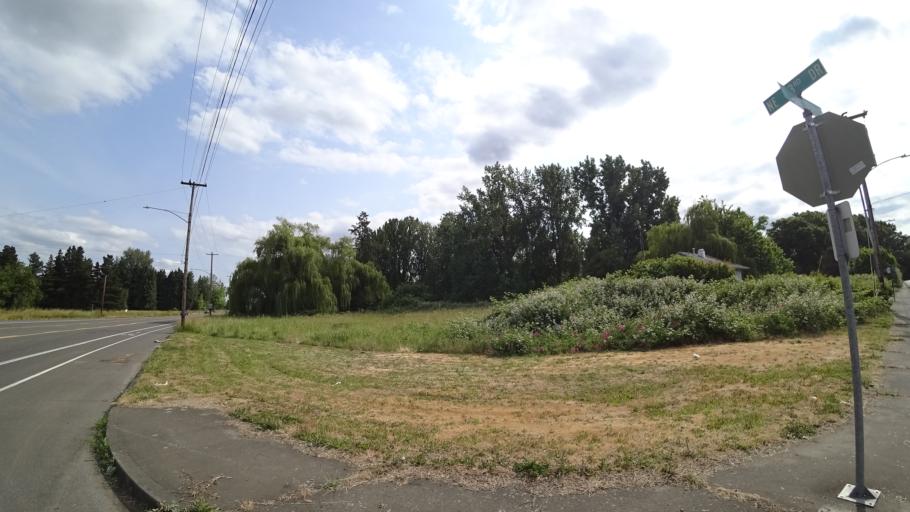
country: US
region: Washington
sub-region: Clark County
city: Vancouver
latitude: 45.5894
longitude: -122.6323
